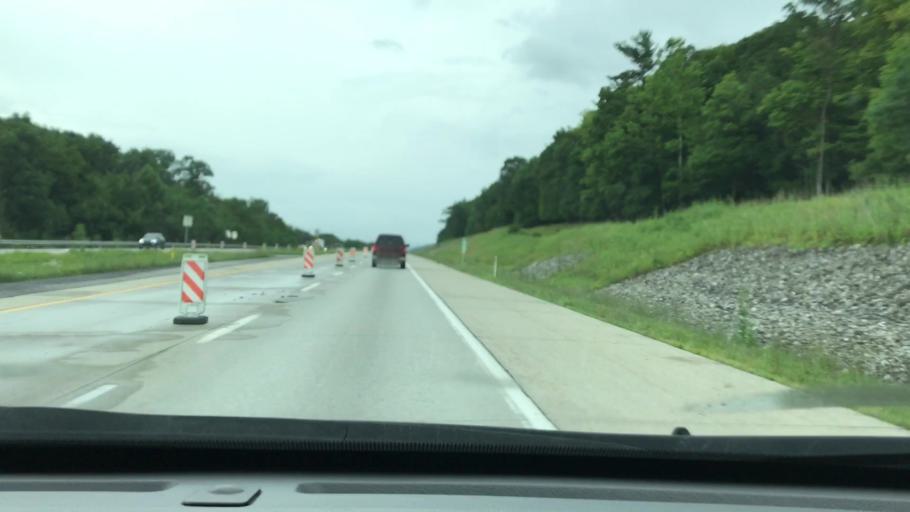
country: US
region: Pennsylvania
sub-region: Blair County
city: Tipton
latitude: 40.6316
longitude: -78.2797
